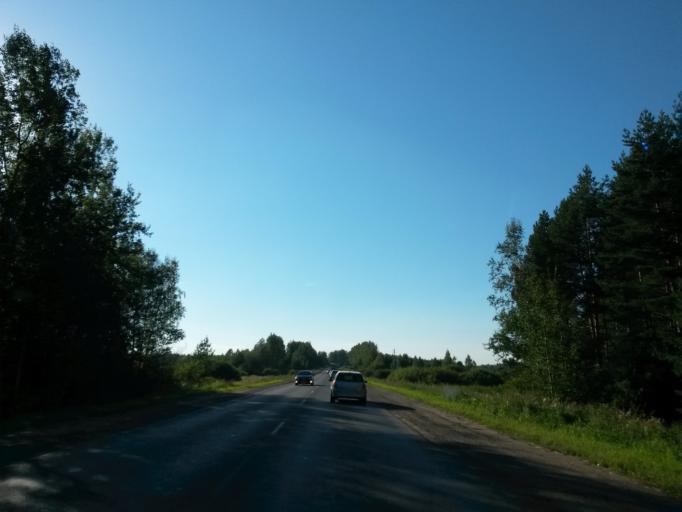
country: RU
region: Ivanovo
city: Novo-Talitsy
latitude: 57.0228
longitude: 40.7677
